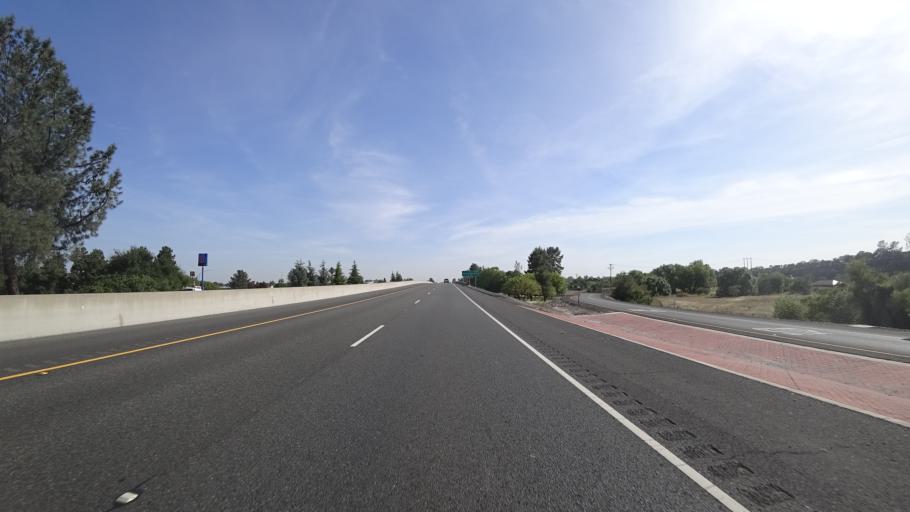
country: US
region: California
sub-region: Butte County
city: Thermalito
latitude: 39.5098
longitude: -121.5730
